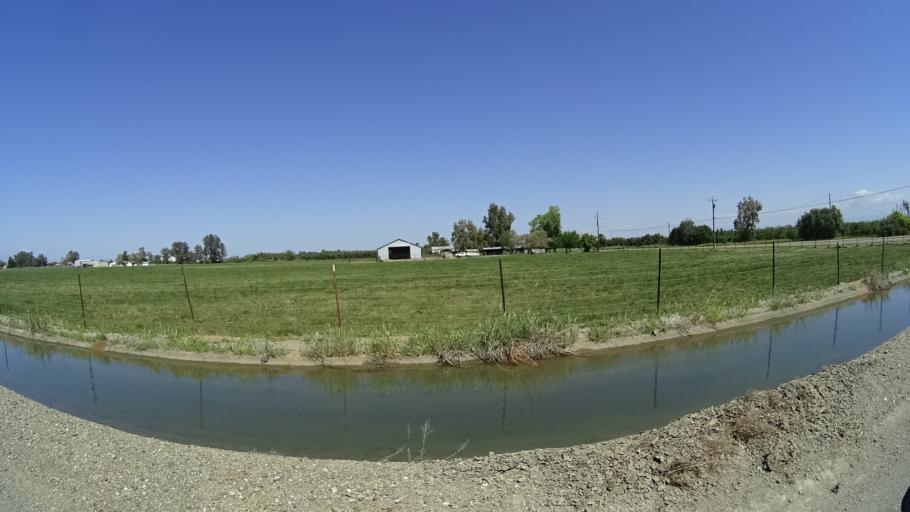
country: US
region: California
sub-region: Glenn County
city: Orland
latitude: 39.7836
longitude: -122.1791
